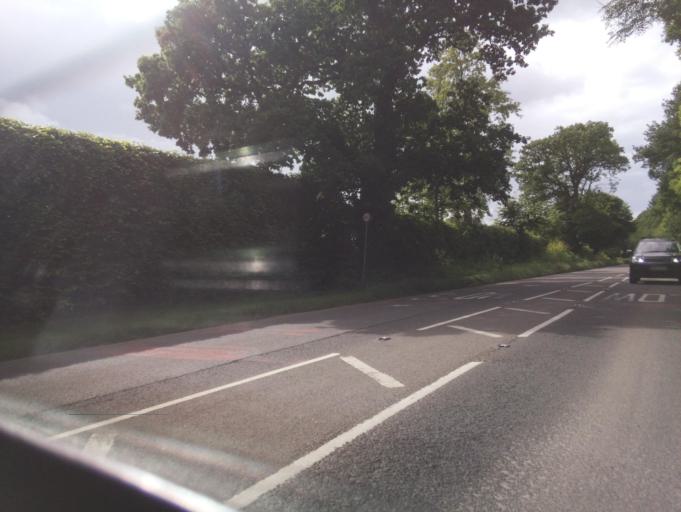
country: GB
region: England
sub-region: Devon
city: Ipplepen
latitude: 50.4963
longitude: -3.6295
